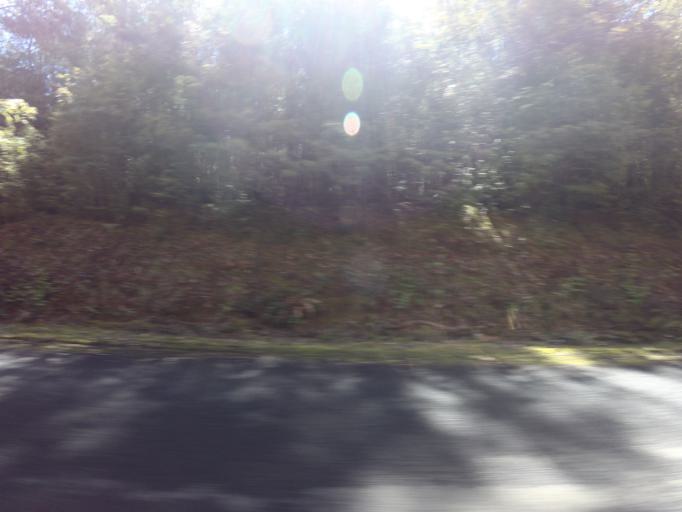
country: AU
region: Tasmania
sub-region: Huon Valley
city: Geeveston
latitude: -42.8205
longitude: 146.2903
